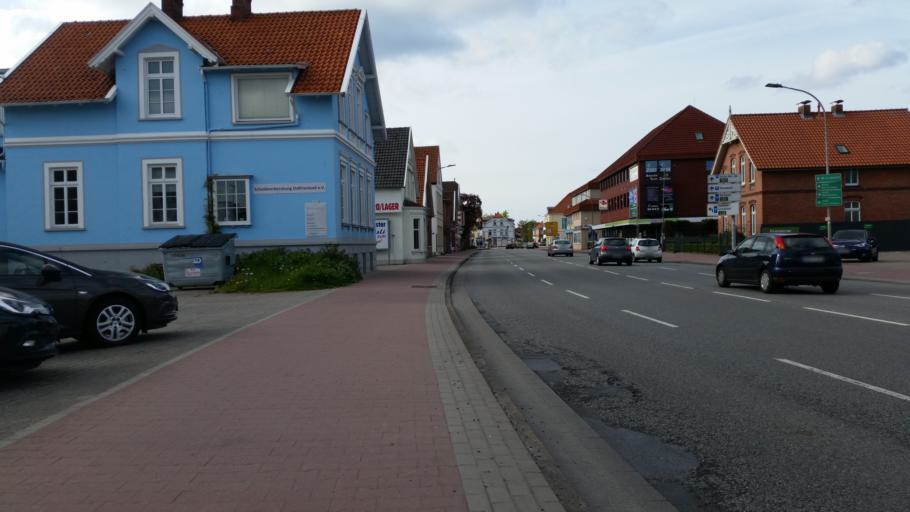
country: DE
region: Lower Saxony
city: Aurich
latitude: 53.4655
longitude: 7.4864
